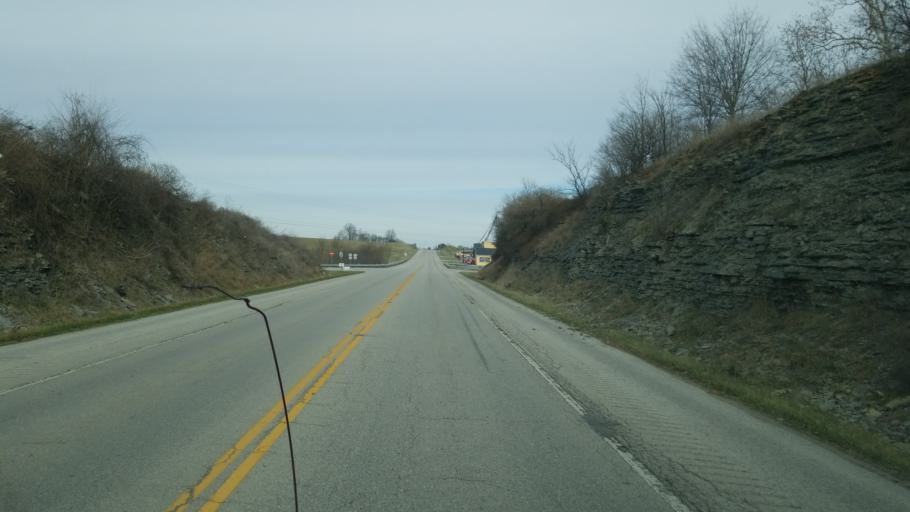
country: US
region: Kentucky
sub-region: Fleming County
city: Flemingsburg
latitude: 38.5230
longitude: -83.8352
